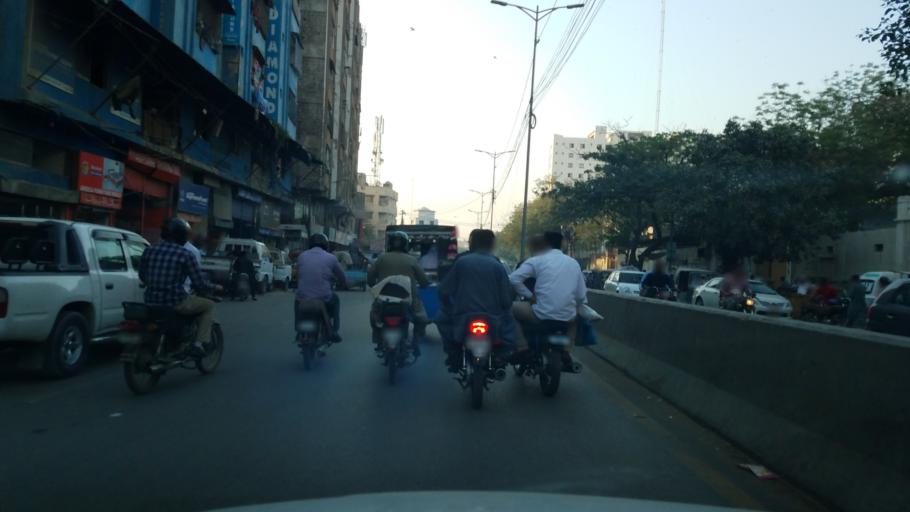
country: PK
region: Sindh
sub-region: Karachi District
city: Karachi
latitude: 24.8673
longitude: 67.0237
